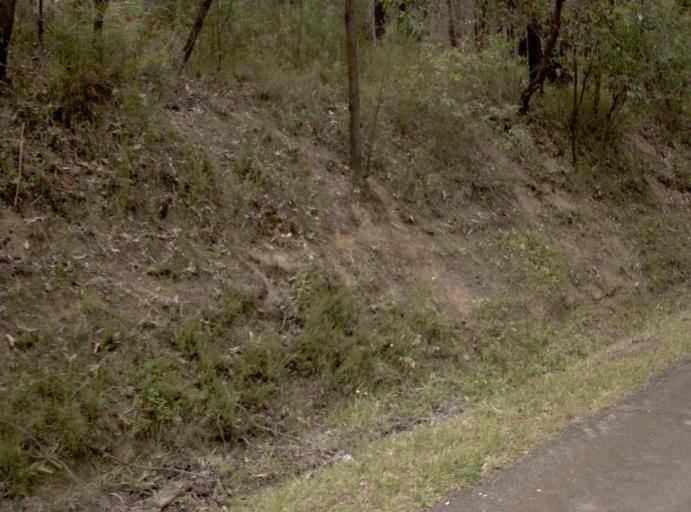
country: AU
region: Victoria
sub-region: Latrobe
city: Moe
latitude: -38.3697
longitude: 146.1795
